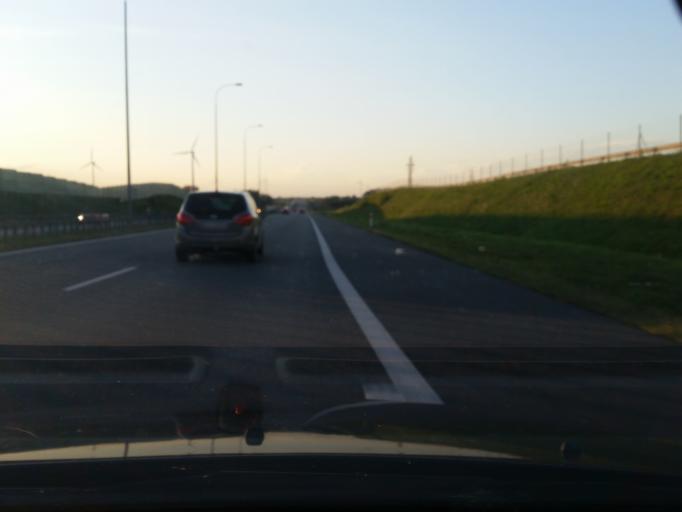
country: PL
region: Kujawsko-Pomorskie
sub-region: Powiat chelminski
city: Lisewo
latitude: 53.3522
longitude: 18.7056
